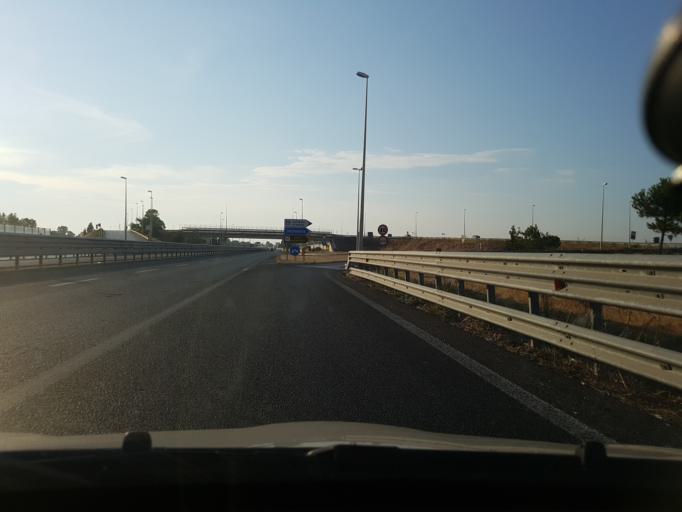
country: IT
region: Apulia
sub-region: Provincia di Foggia
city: Carapelle
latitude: 41.3929
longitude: 15.6623
